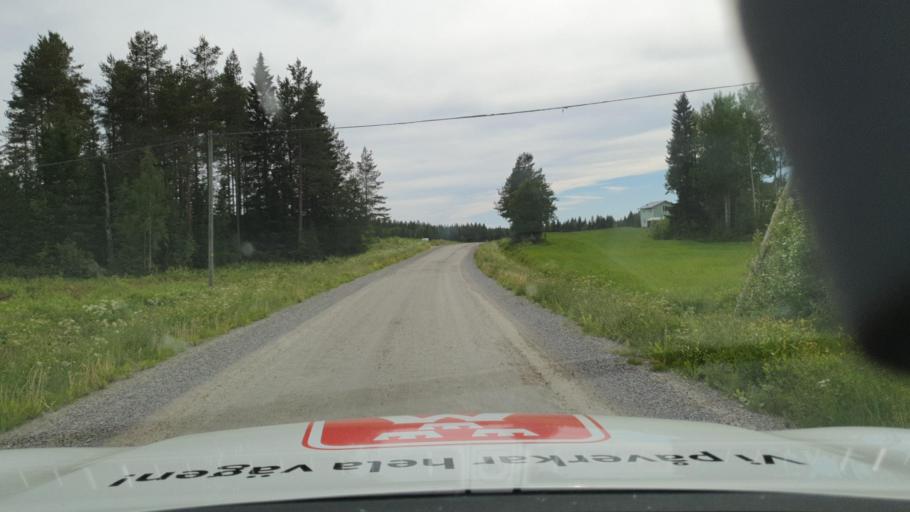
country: SE
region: Vaesterbotten
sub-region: Skelleftea Kommun
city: Burea
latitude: 64.4618
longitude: 21.0393
